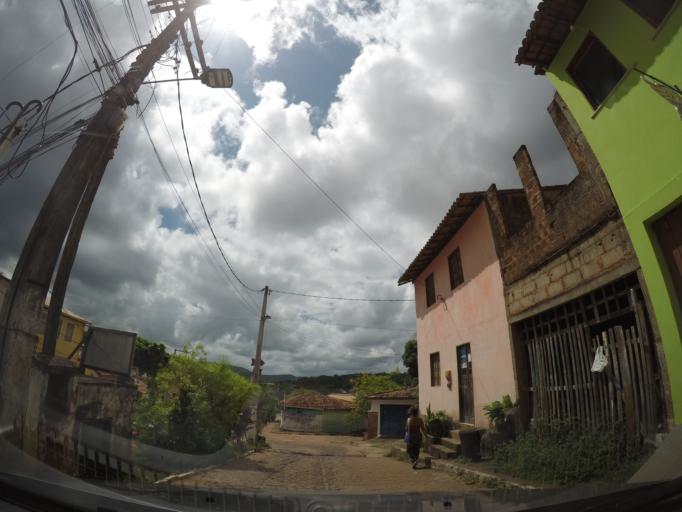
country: BR
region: Bahia
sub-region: Andarai
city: Vera Cruz
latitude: -12.5611
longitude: -41.3891
